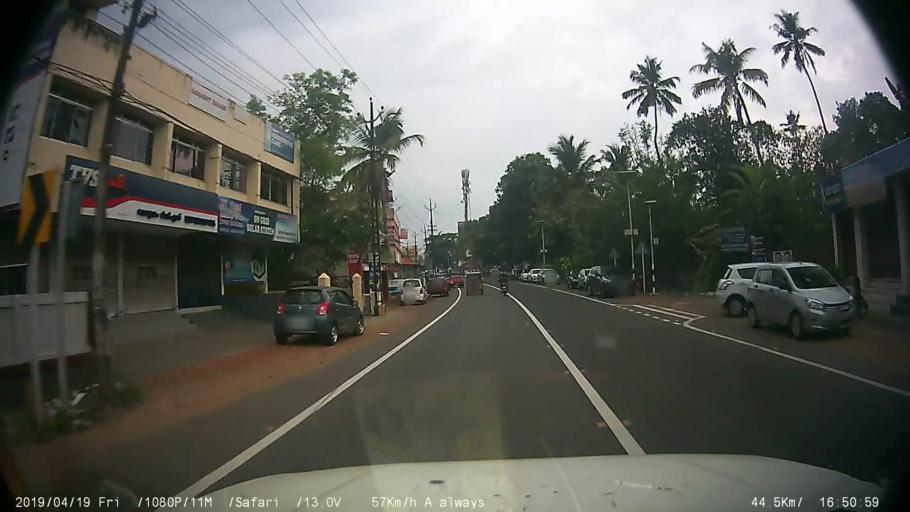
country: IN
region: Kerala
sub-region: Kottayam
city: Changanacheri
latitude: 9.4597
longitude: 76.5335
